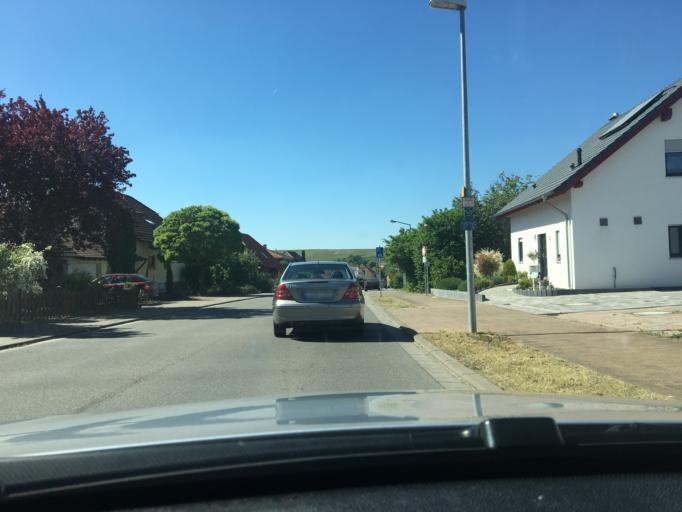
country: DE
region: Rheinland-Pfalz
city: Wollstein
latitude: 49.8094
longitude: 7.9649
